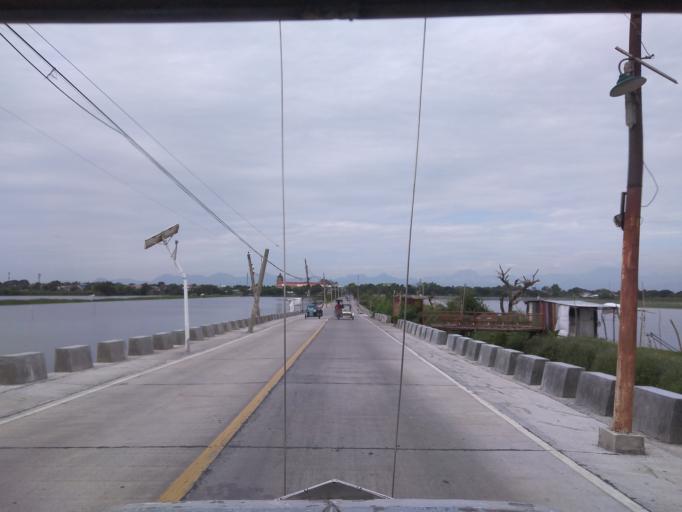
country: PH
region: Central Luzon
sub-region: Province of Pampanga
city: Lubao
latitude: 14.9383
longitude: 120.6086
